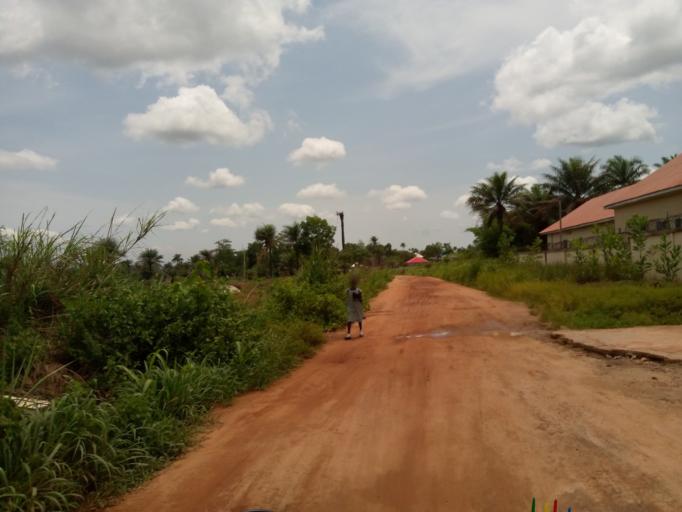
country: SL
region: Western Area
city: Waterloo
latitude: 8.3520
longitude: -12.9579
